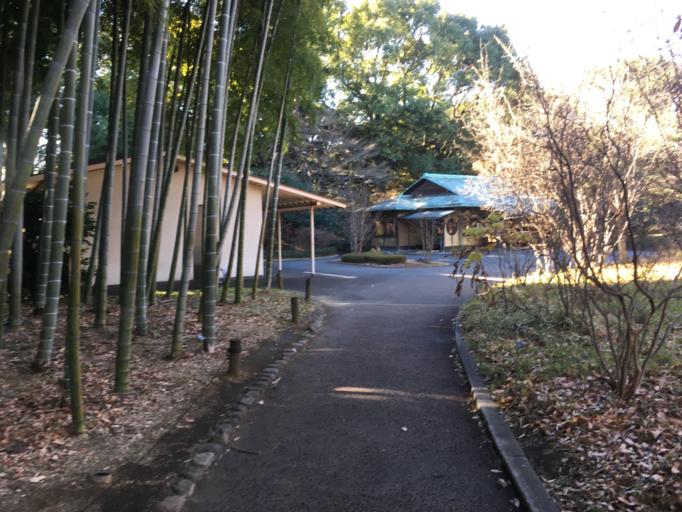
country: JP
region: Tokyo
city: Tokyo
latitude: 35.6868
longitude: 139.7581
